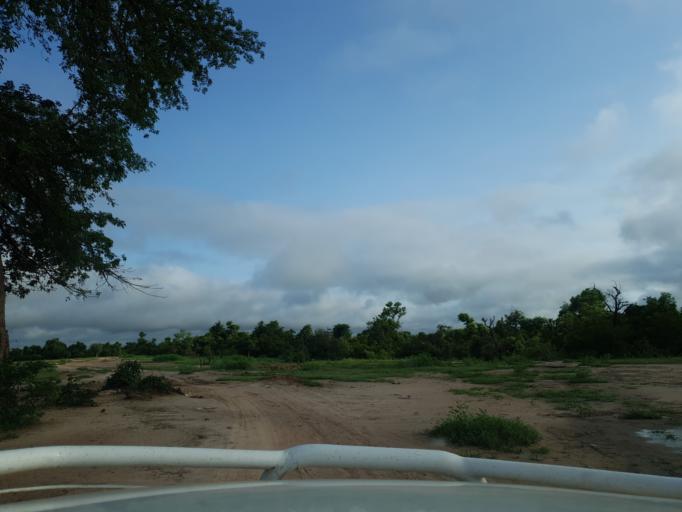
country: ML
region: Segou
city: Baroueli
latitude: 13.3880
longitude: -7.0059
